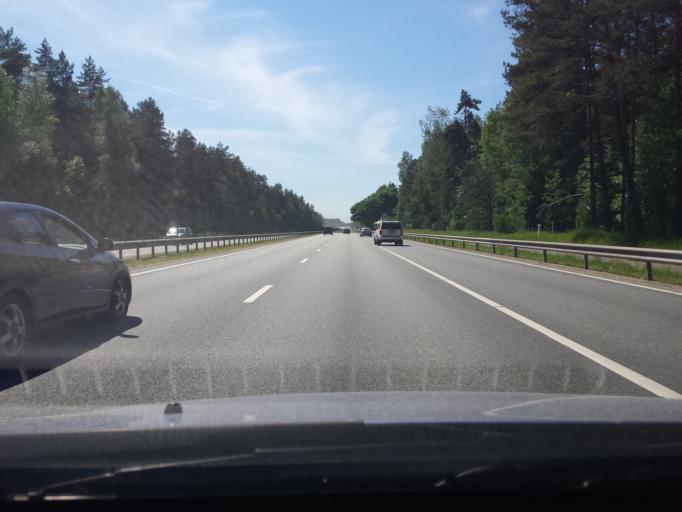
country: LV
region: Riga
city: Bergi
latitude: 57.0087
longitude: 24.3027
